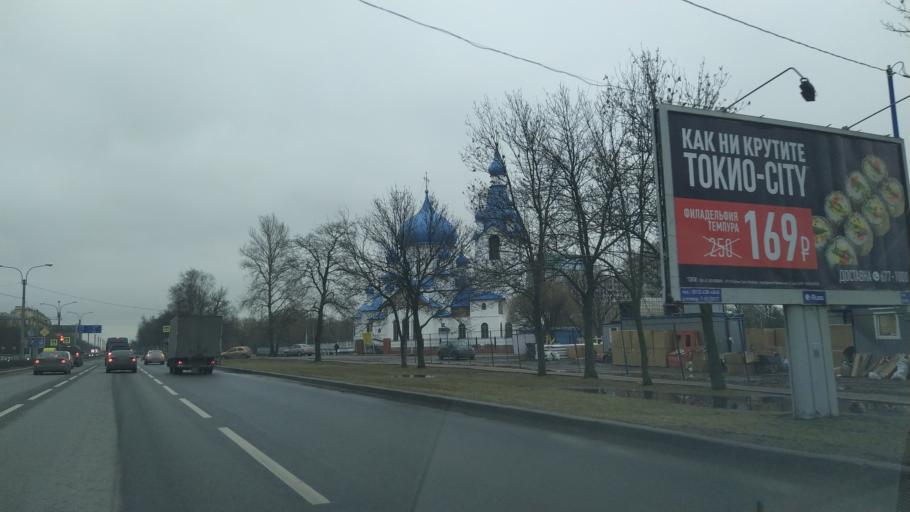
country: RU
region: St.-Petersburg
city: Kupchino
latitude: 59.8378
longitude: 30.3313
